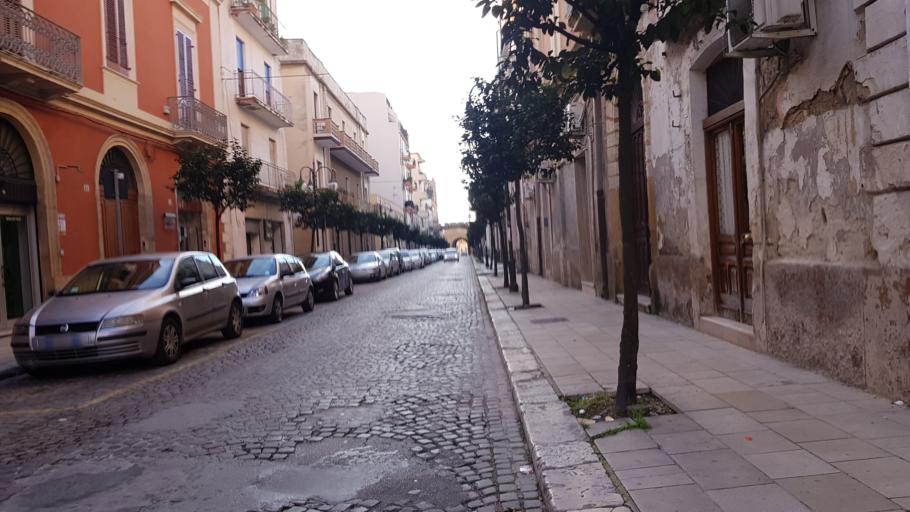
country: IT
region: Apulia
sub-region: Provincia di Brindisi
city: Brindisi
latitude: 40.6349
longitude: 17.9450
